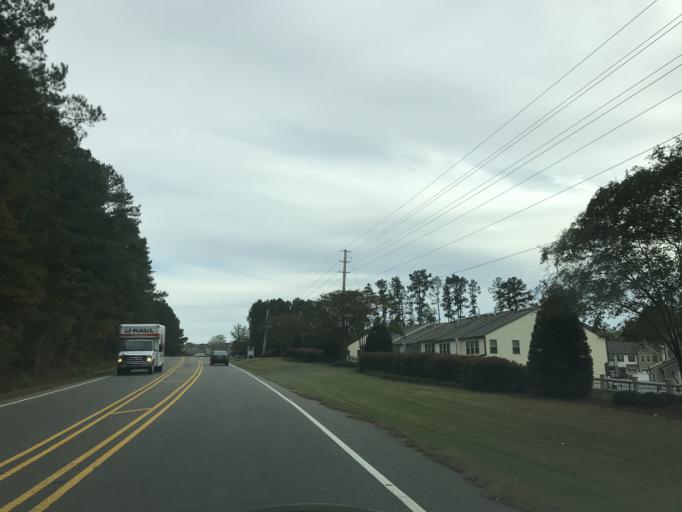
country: US
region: North Carolina
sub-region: Wake County
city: Rolesville
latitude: 35.9140
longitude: -78.5061
